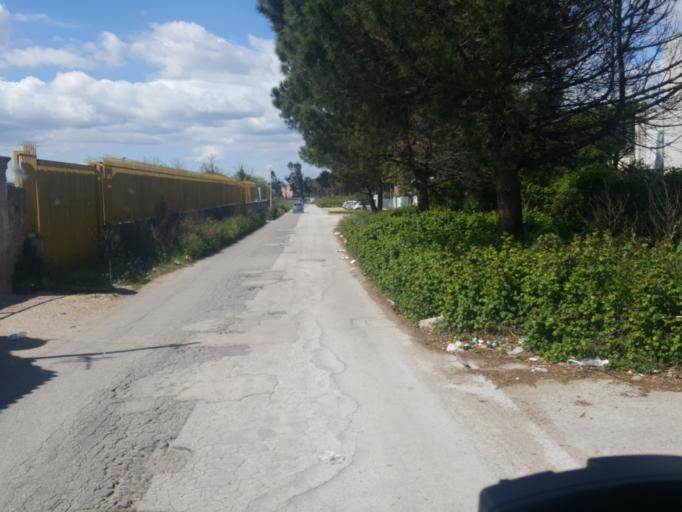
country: IT
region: Campania
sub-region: Provincia di Napoli
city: Torretta-Scalzapecora
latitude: 40.9332
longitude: 14.1060
